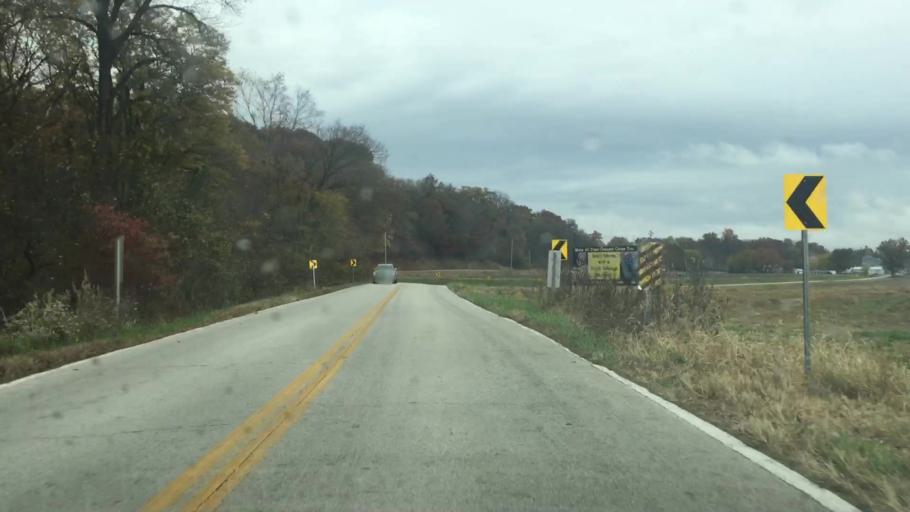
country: US
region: Missouri
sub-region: Gasconade County
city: Hermann
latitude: 38.7143
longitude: -91.5297
